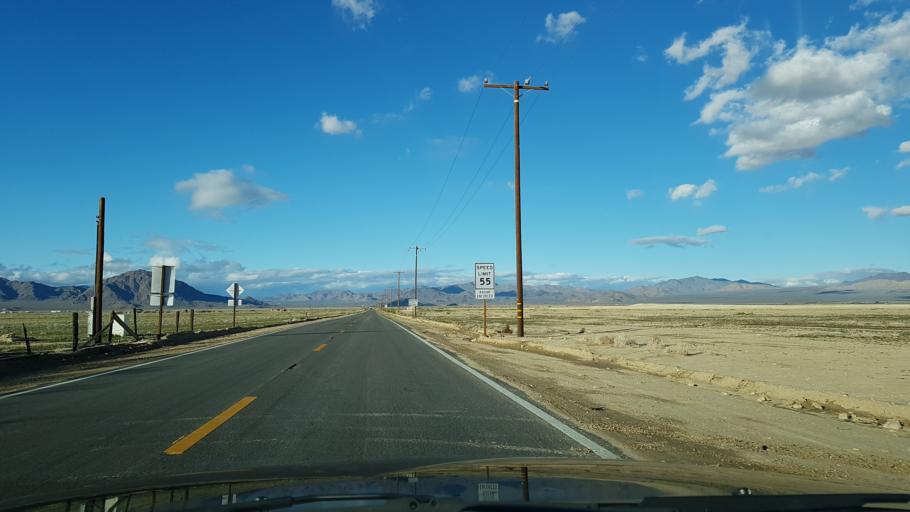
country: US
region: California
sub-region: San Bernardino County
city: Lucerne Valley
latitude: 34.4593
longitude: -116.9457
